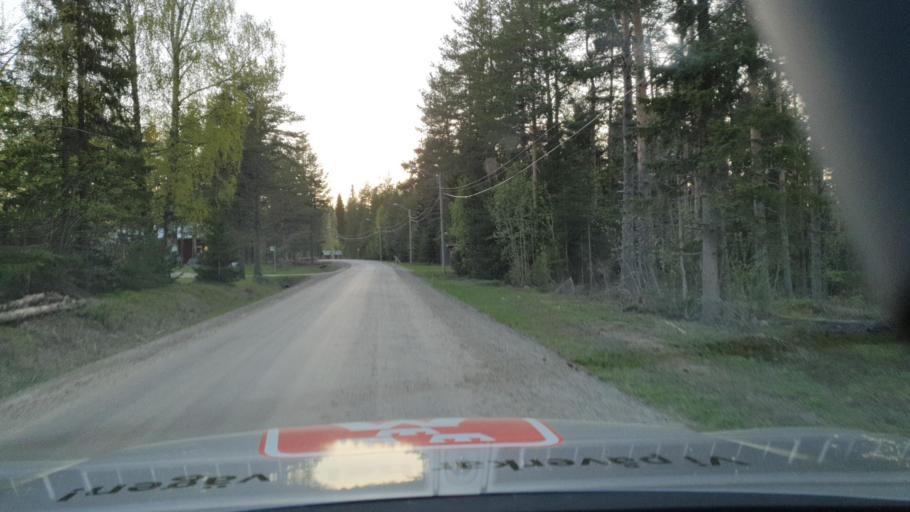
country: SE
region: Vaesternorrland
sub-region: OErnskoeldsviks Kommun
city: Ornskoldsvik
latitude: 63.5276
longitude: 18.5779
